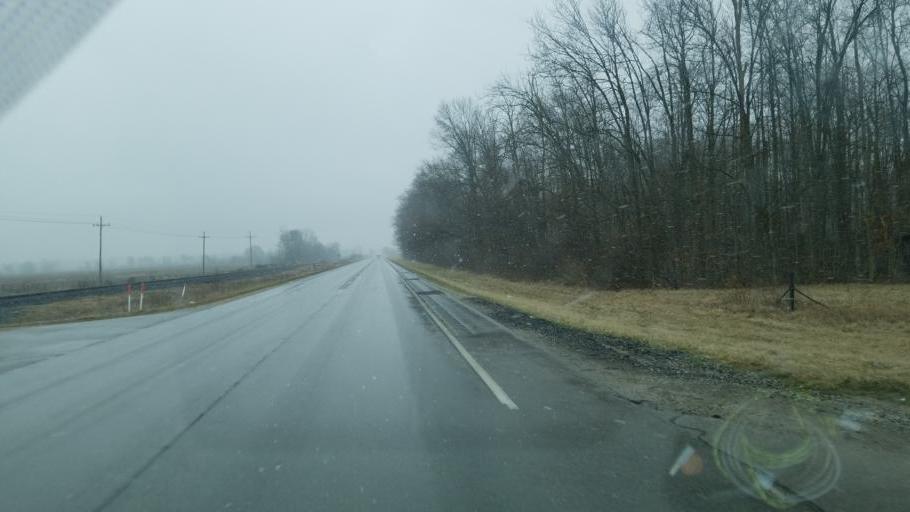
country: US
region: Indiana
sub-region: Wabash County
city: Mount Vernon
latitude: 40.6958
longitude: -85.7494
